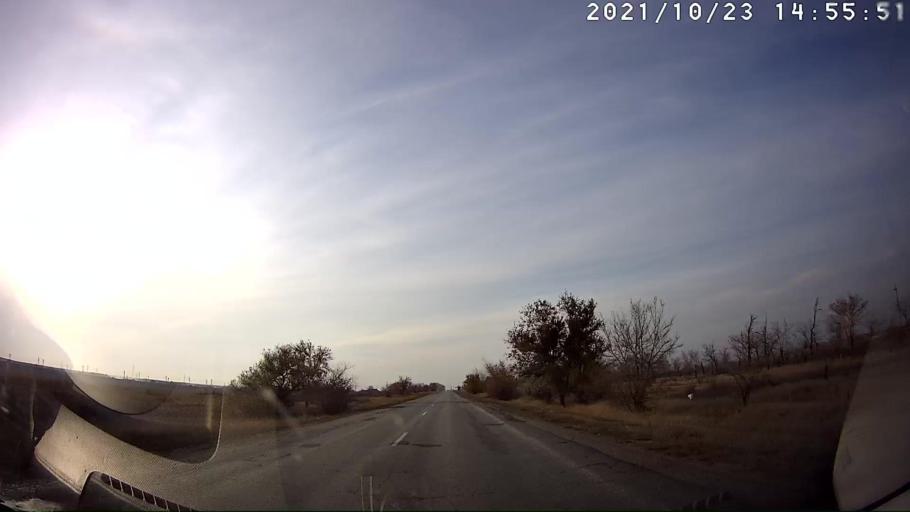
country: RU
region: Volgograd
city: Volgograd
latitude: 48.4552
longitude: 44.3869
